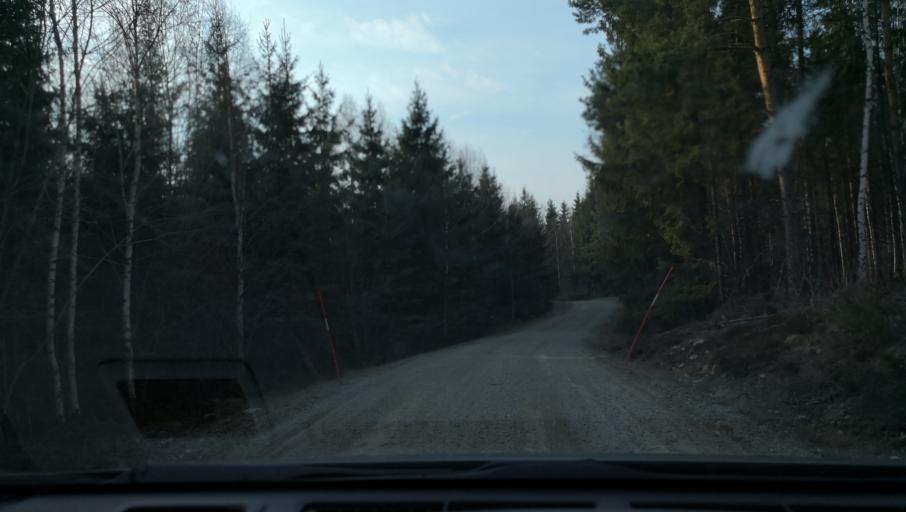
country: SE
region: OErebro
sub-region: Orebro Kommun
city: Hovsta
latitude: 59.3794
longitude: 15.2994
